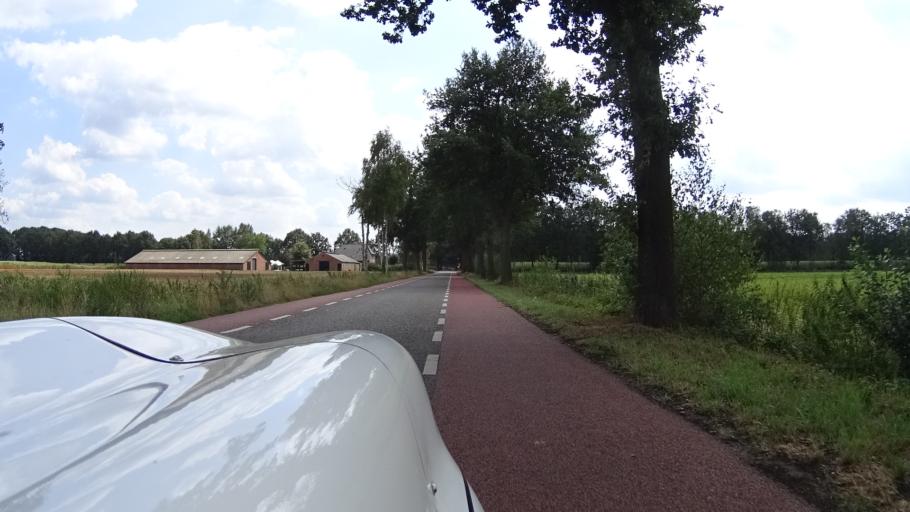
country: NL
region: North Brabant
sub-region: Gemeente Bernheze
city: Loosbroek
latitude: 51.6802
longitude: 5.4625
